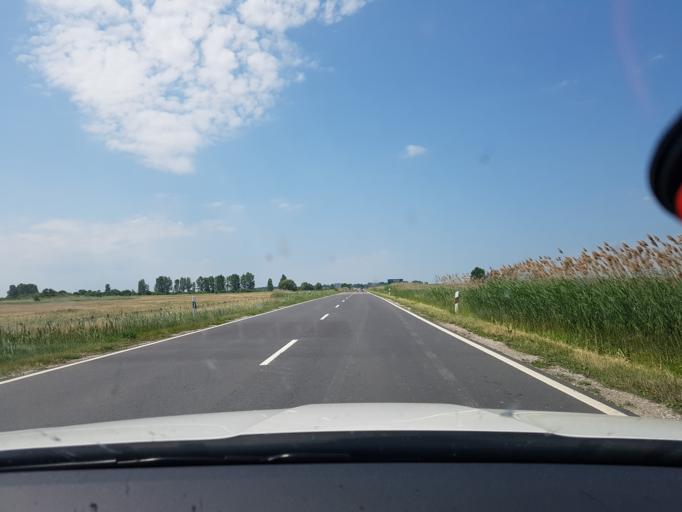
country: HU
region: Hajdu-Bihar
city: Hortobagy
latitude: 47.5889
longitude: 21.0357
